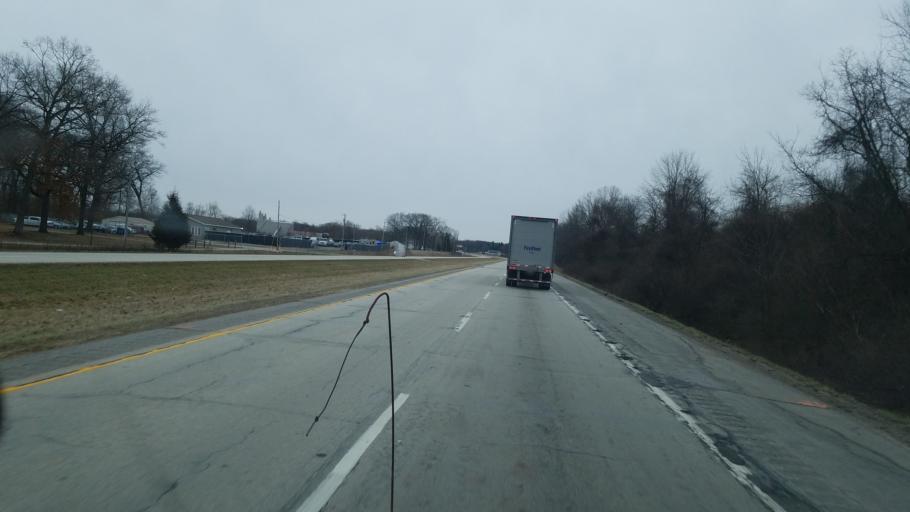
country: US
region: Indiana
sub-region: Starke County
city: Koontz Lake
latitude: 41.3658
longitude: -86.4741
